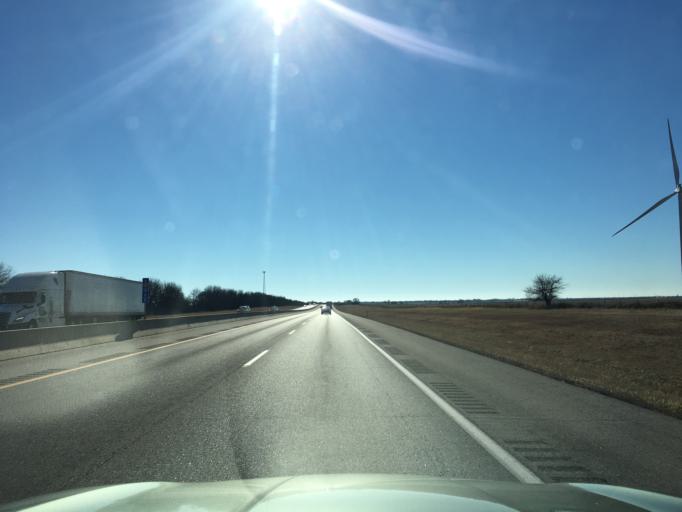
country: US
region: Kansas
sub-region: Sumner County
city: Wellington
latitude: 37.1266
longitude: -97.3390
